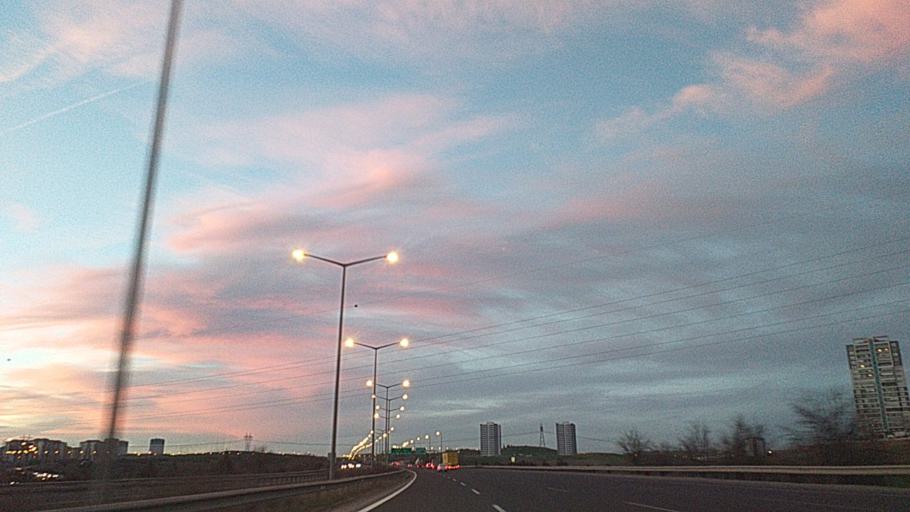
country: TR
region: Ankara
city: Etimesgut
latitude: 40.0015
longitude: 32.6357
